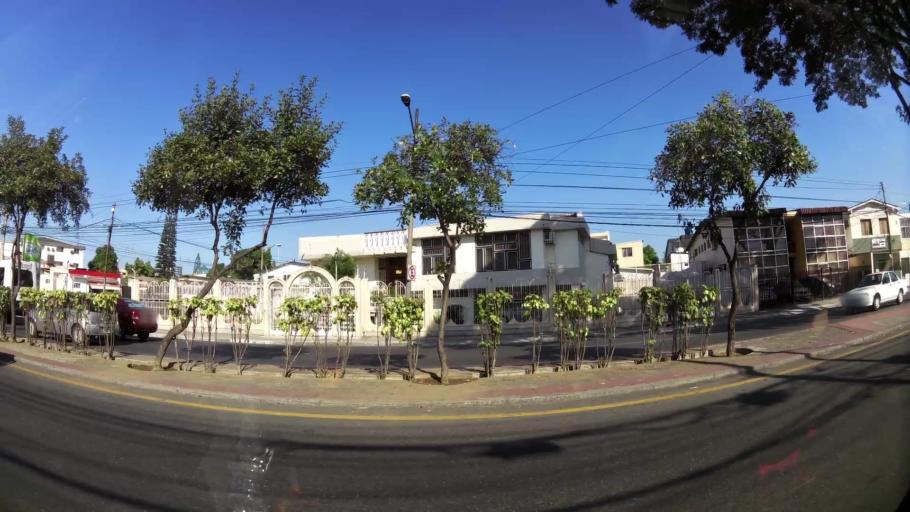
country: EC
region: Guayas
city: Guayaquil
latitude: -2.1774
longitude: -79.8977
